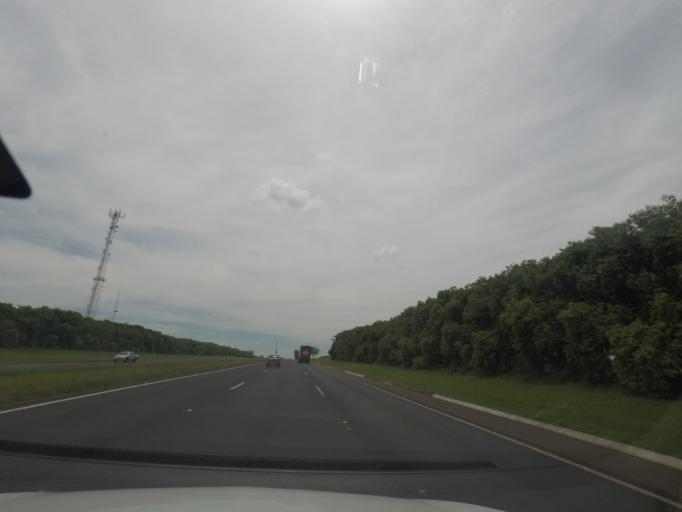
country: BR
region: Sao Paulo
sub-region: Bebedouro
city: Bebedouro
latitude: -20.9910
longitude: -48.4335
